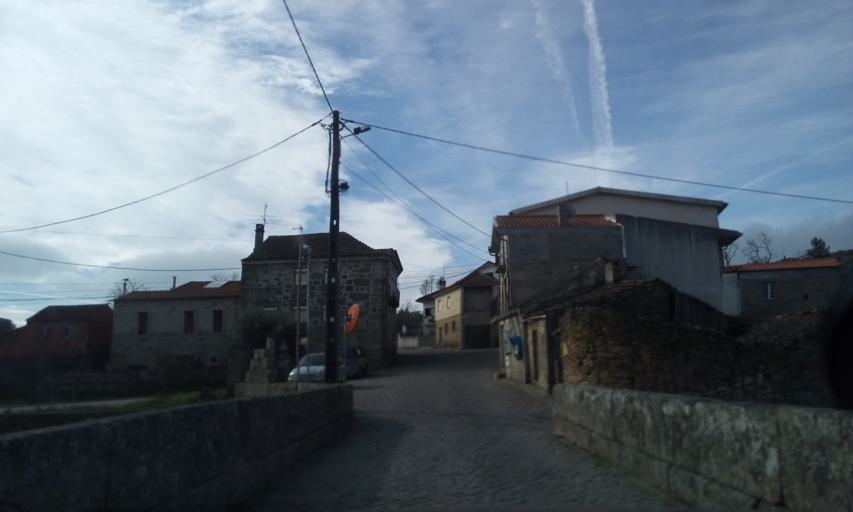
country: PT
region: Guarda
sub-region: Fornos de Algodres
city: Fornos de Algodres
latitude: 40.6812
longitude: -7.5306
